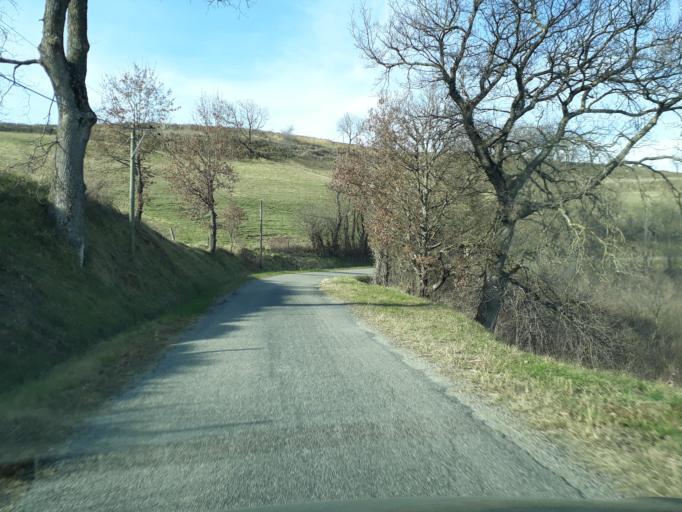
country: FR
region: Midi-Pyrenees
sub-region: Departement de la Haute-Garonne
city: Montesquieu-Volvestre
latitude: 43.1790
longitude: 1.2896
